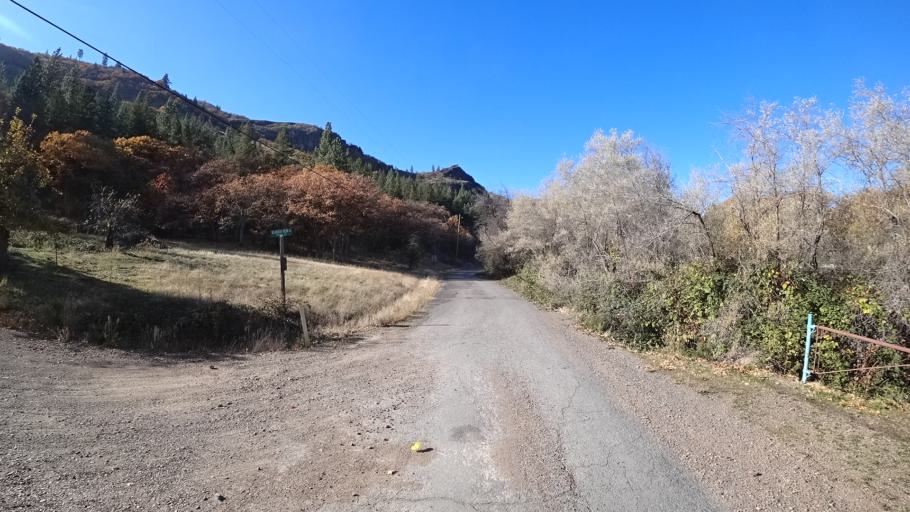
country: US
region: California
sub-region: Siskiyou County
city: Montague
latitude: 41.9644
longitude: -122.2592
